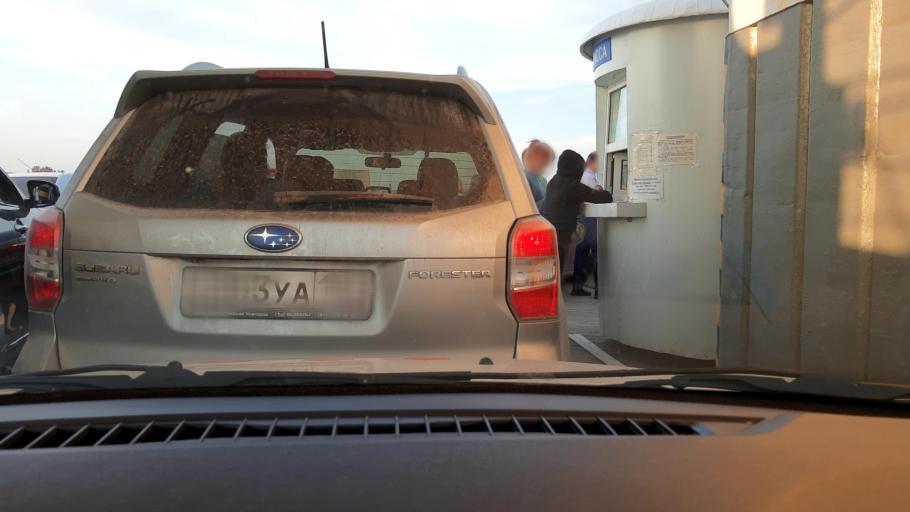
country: RU
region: Nizjnij Novgorod
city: Nizhniy Novgorod
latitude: 56.3362
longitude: 44.0278
